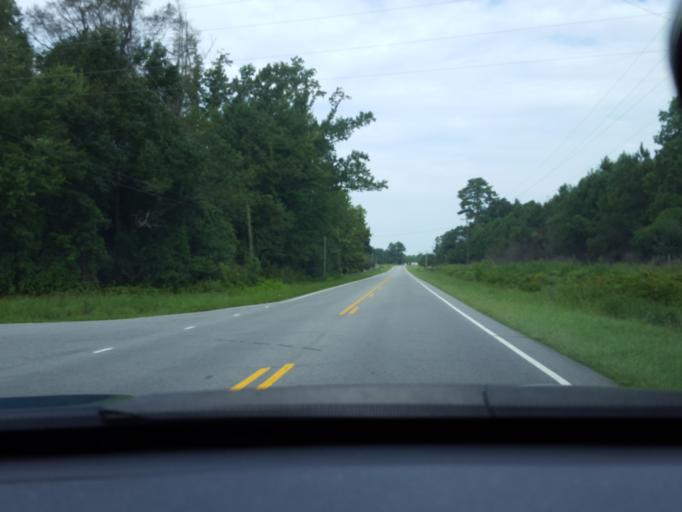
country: US
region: North Carolina
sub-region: Chowan County
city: Edenton
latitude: 36.1295
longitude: -76.6536
